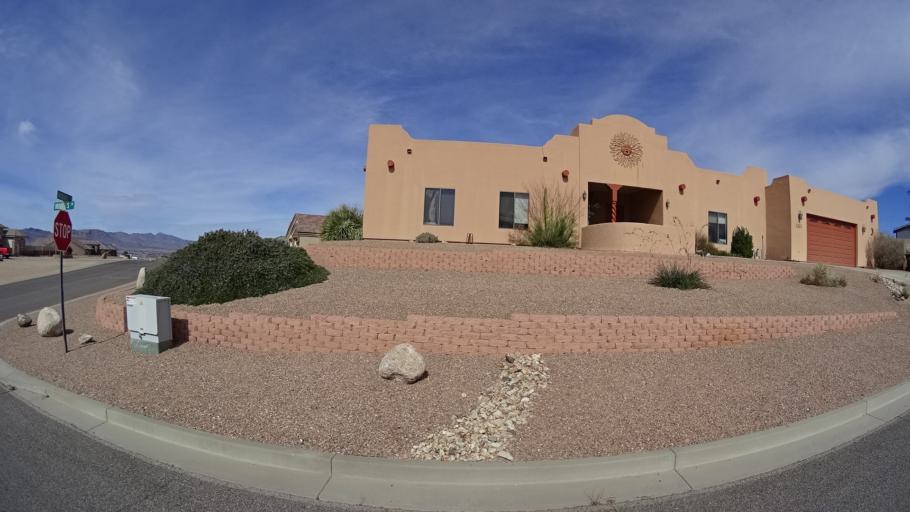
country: US
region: Arizona
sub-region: Mohave County
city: Kingman
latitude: 35.1906
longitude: -113.9809
